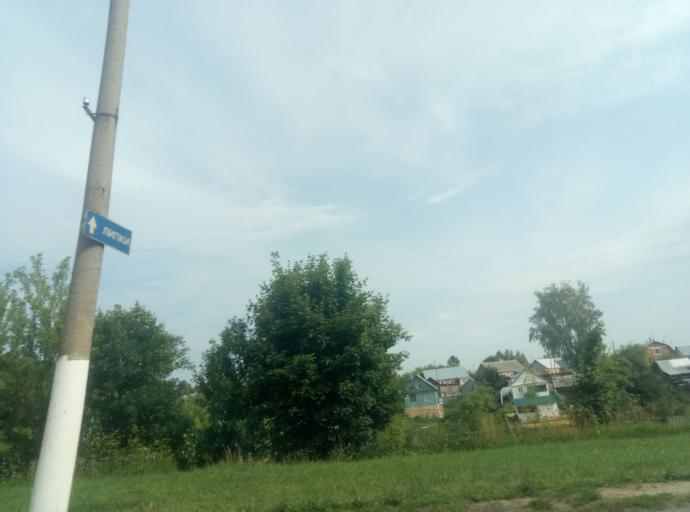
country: RU
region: Tula
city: Kireyevsk
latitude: 53.9327
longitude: 37.9390
